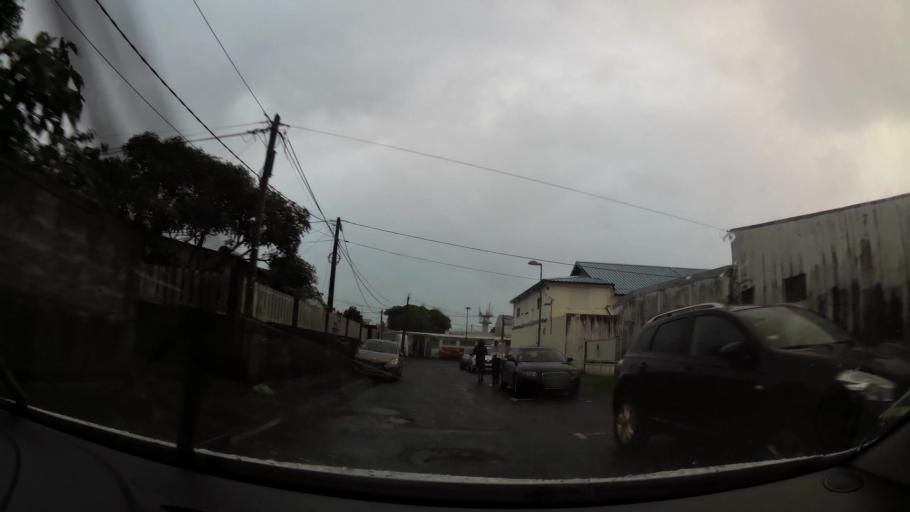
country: RE
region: Reunion
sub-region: Reunion
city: Saint-Benoit
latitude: -21.0415
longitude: 55.7194
